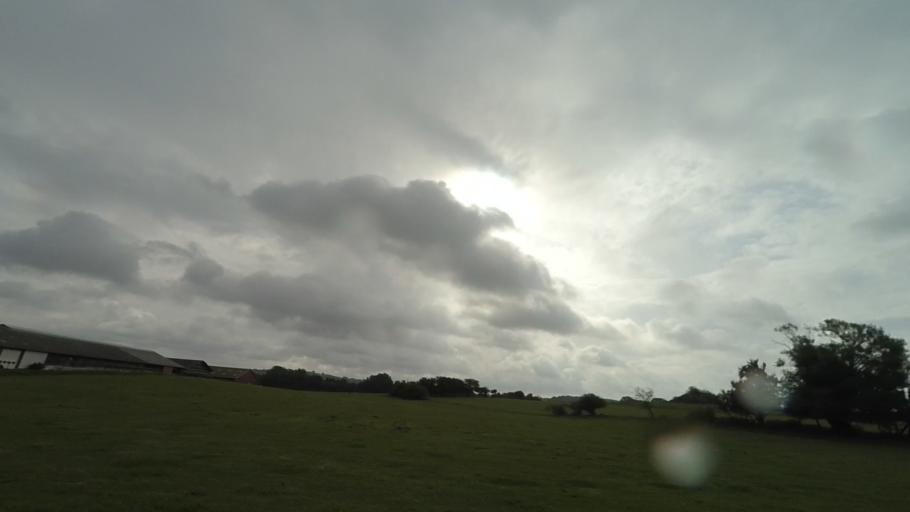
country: DK
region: Central Jutland
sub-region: Syddjurs Kommune
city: Ronde
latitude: 56.2990
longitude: 10.4447
